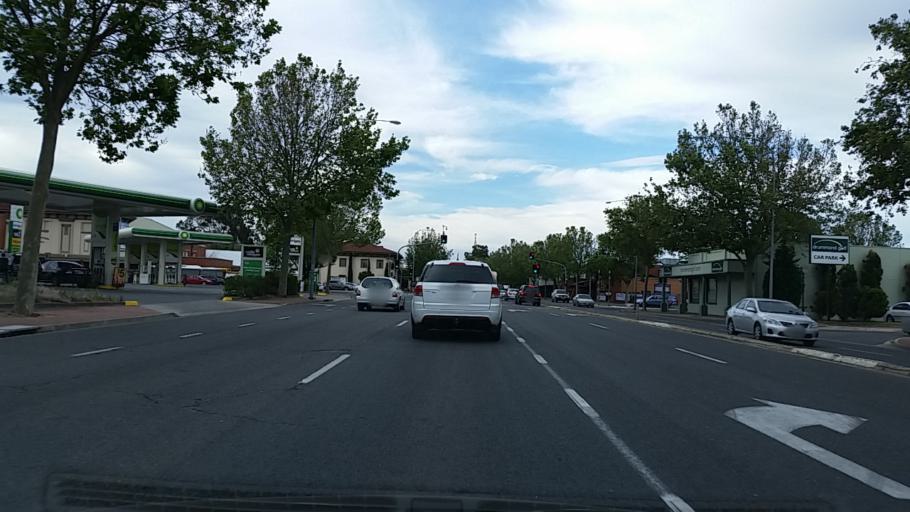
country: AU
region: South Australia
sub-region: City of West Torrens
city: Thebarton
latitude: -34.9247
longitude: 138.5698
